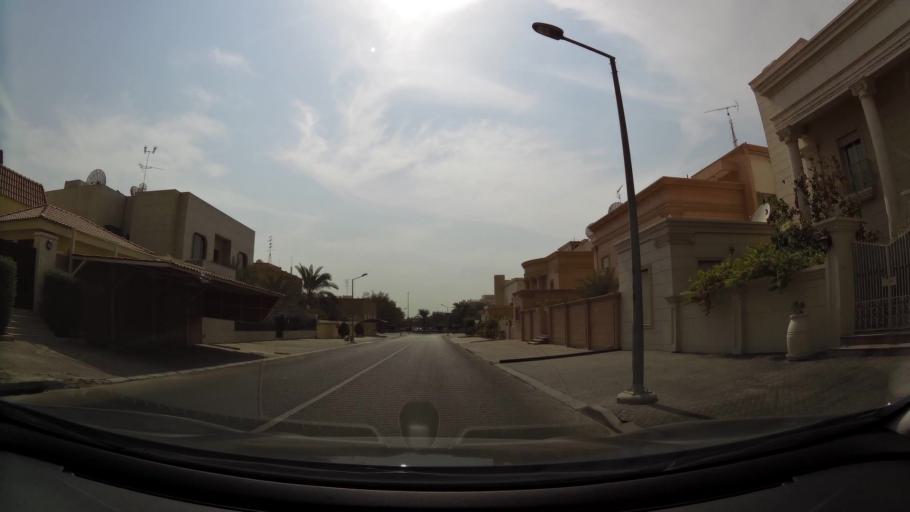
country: KW
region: Al Asimah
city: Kuwait City
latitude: 29.3547
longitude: 47.9759
